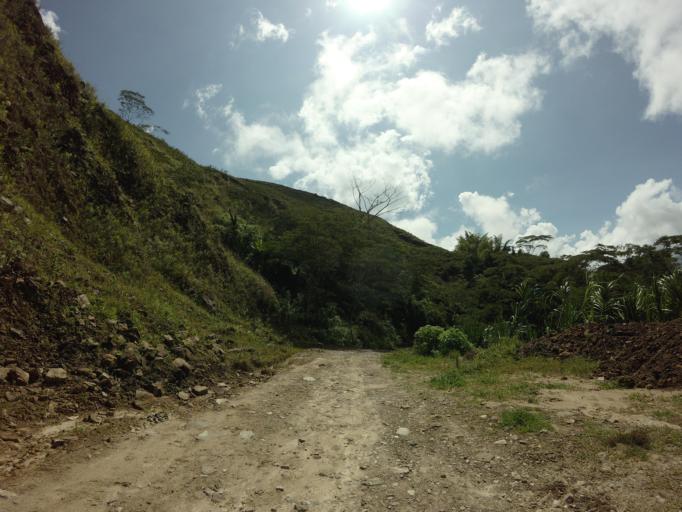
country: CO
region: Antioquia
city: Narino
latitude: 5.5098
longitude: -75.1750
